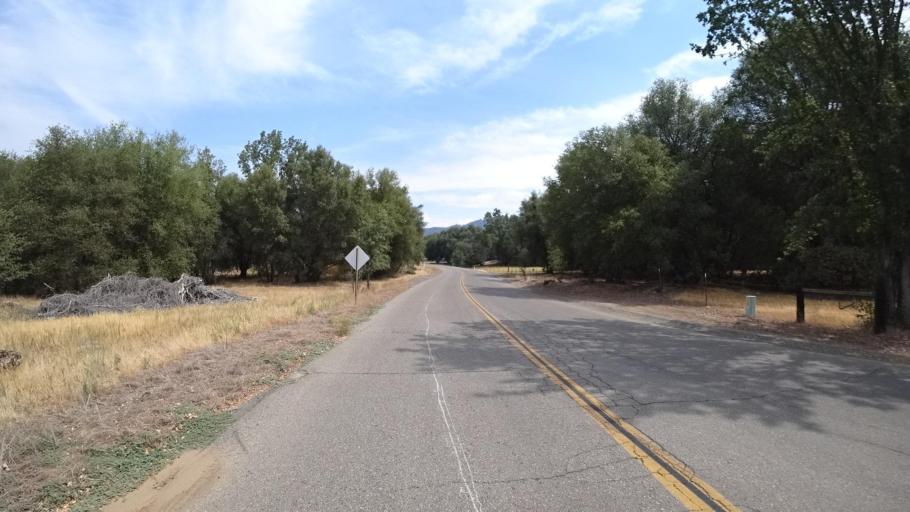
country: US
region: California
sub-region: Mariposa County
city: Midpines
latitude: 37.4864
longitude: -119.8924
